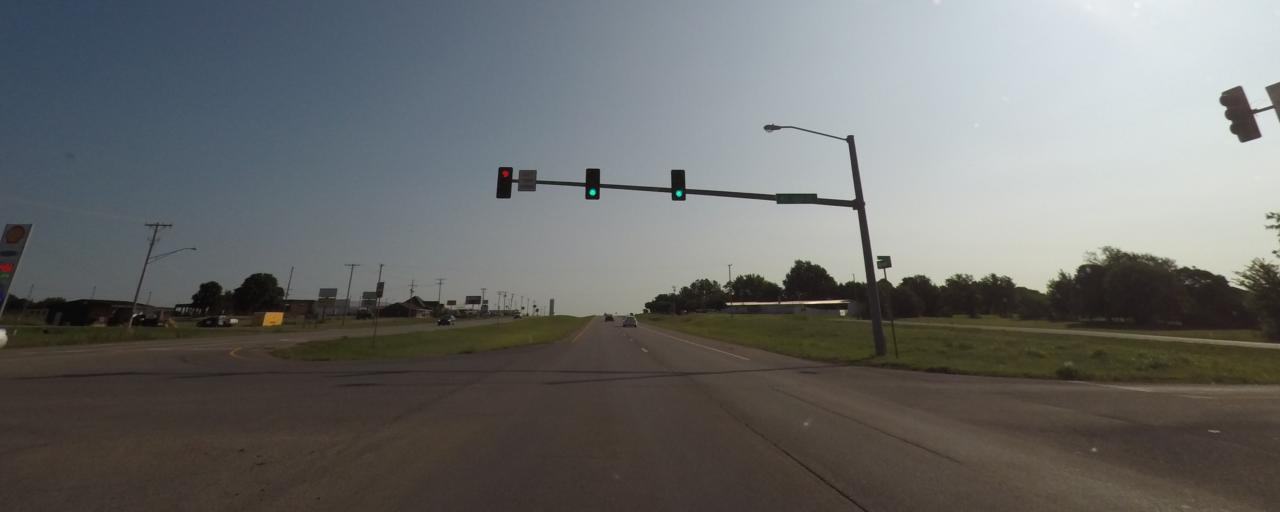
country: US
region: Oklahoma
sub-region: McClain County
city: Blanchard
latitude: 35.1454
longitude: -97.6423
